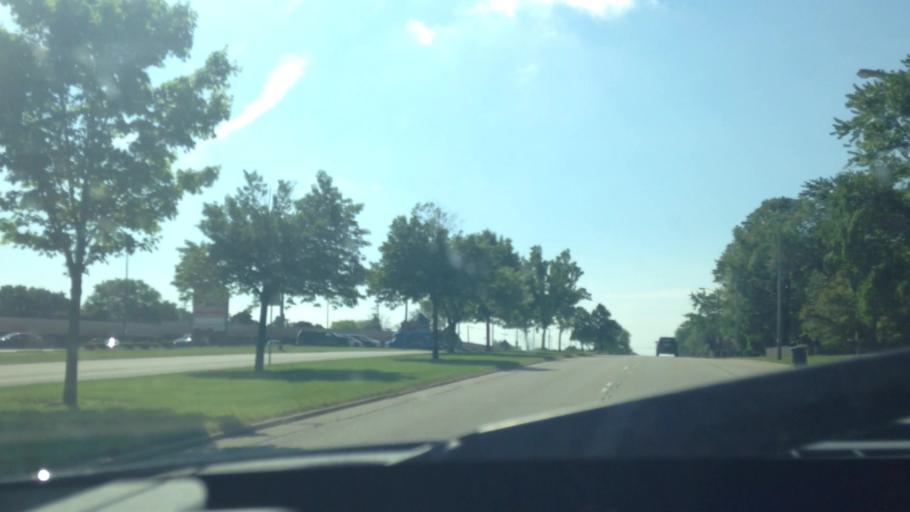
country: US
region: Wisconsin
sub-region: Waukesha County
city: Menomonee Falls
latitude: 43.1665
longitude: -88.0996
